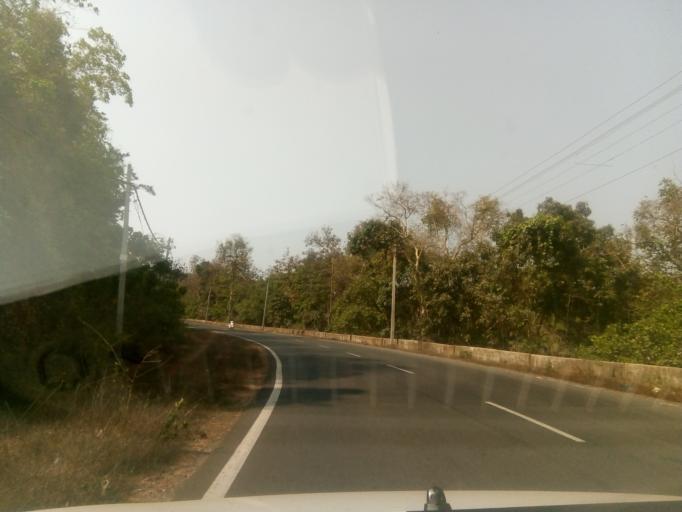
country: IN
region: Goa
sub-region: North Goa
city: Pernem
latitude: 15.6996
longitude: 73.8500
